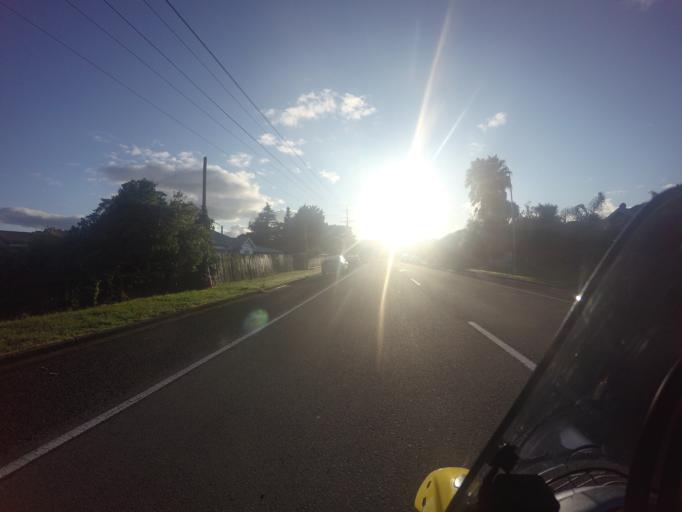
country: NZ
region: Gisborne
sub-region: Gisborne District
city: Gisborne
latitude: -38.6736
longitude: 178.0381
